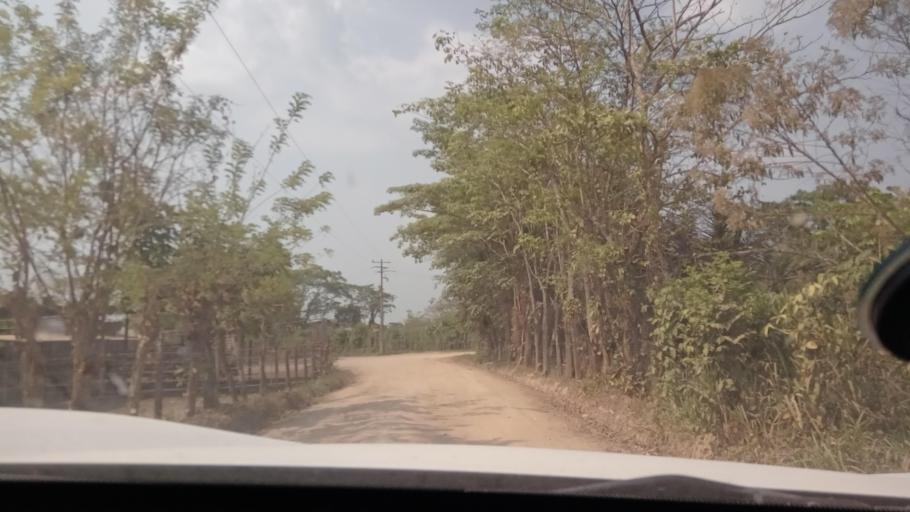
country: MX
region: Tabasco
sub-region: Huimanguillo
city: Francisco Rueda
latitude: 17.6826
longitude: -93.8619
